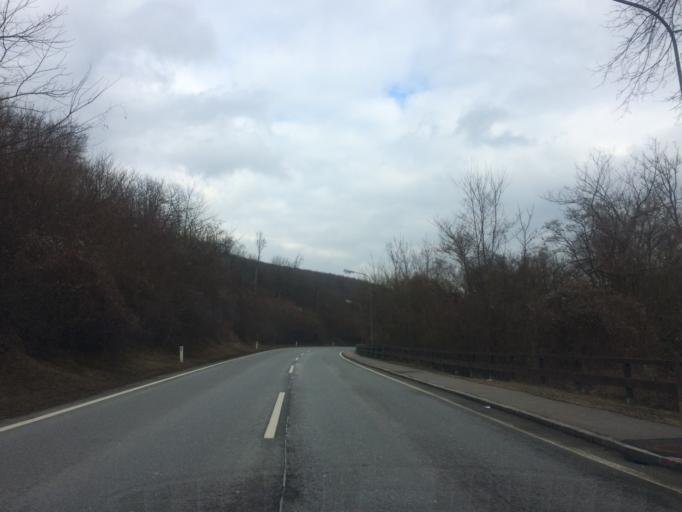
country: AT
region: Lower Austria
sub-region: Politischer Bezirk Wien-Umgebung
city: Purkersdorf
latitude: 48.1992
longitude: 16.1533
